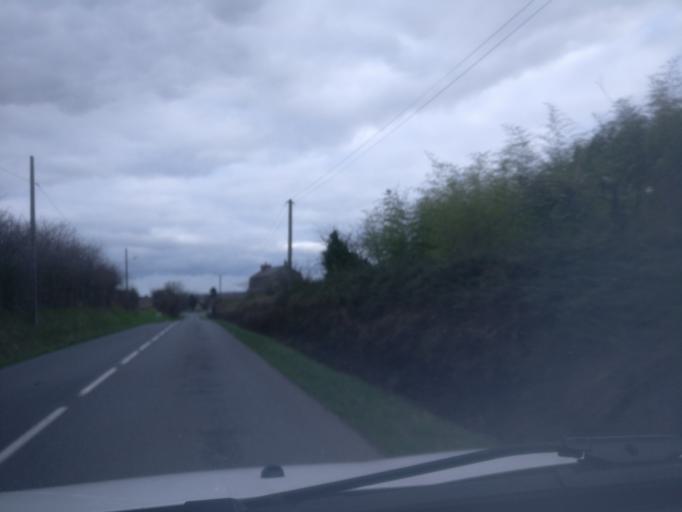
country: FR
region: Lower Normandy
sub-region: Departement de la Manche
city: Marcey-les-Greves
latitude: 48.6846
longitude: -1.3833
